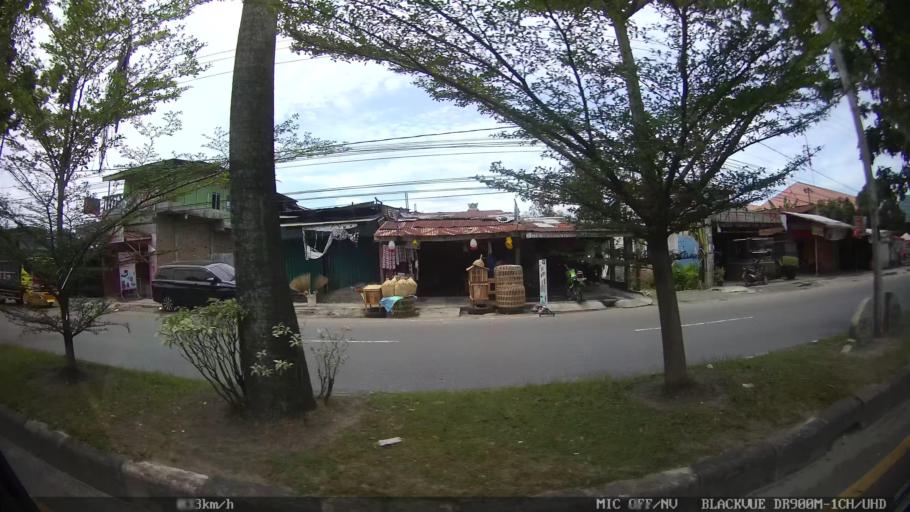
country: ID
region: North Sumatra
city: Sunggal
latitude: 3.5279
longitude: 98.6351
